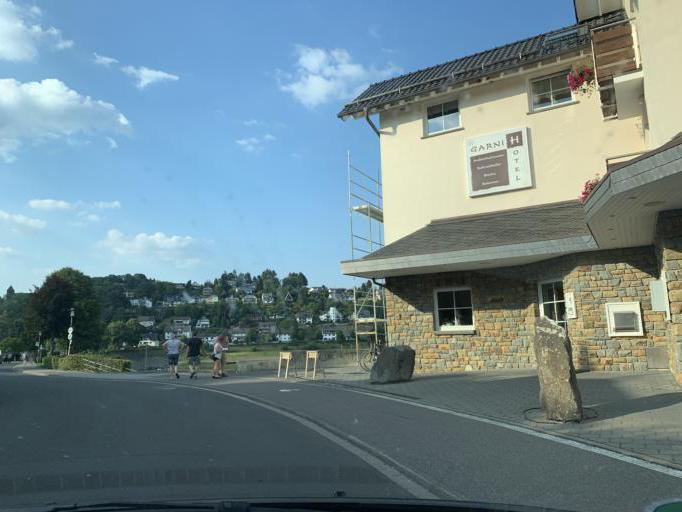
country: DE
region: North Rhine-Westphalia
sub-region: Regierungsbezirk Koln
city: Simmerath
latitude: 50.6088
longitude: 6.3855
